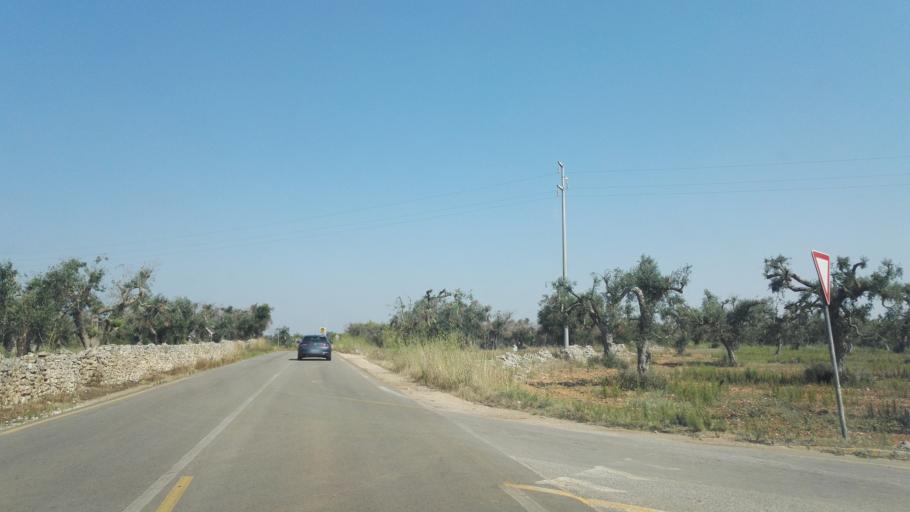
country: IT
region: Apulia
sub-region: Provincia di Lecce
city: Nardo
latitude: 40.1828
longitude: 17.9734
